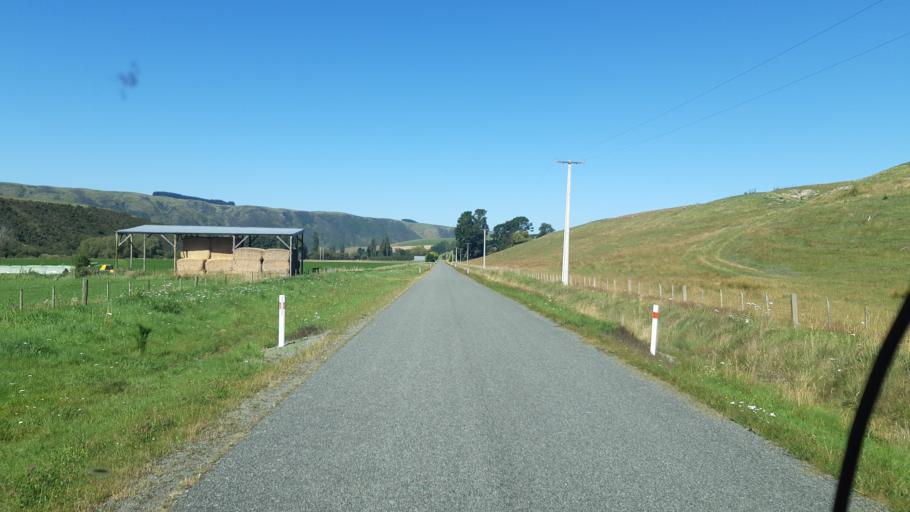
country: NZ
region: Canterbury
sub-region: Timaru District
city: Pleasant Point
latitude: -44.2885
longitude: 170.8790
